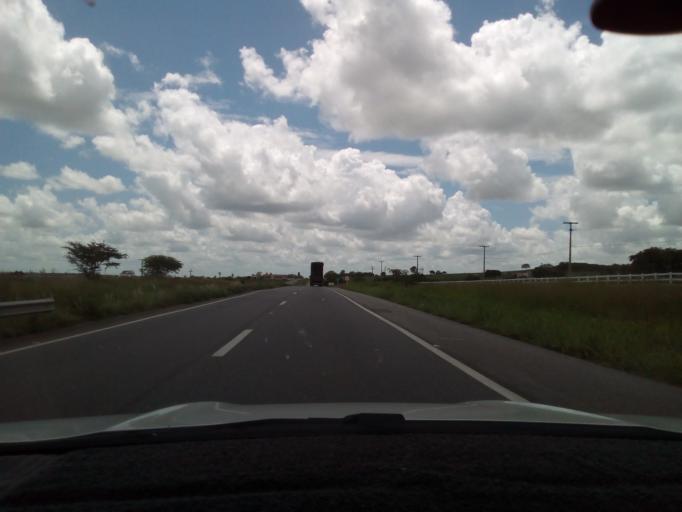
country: BR
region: Paraiba
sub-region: Gurinhem
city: Gurinhem
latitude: -7.1705
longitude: -35.3809
